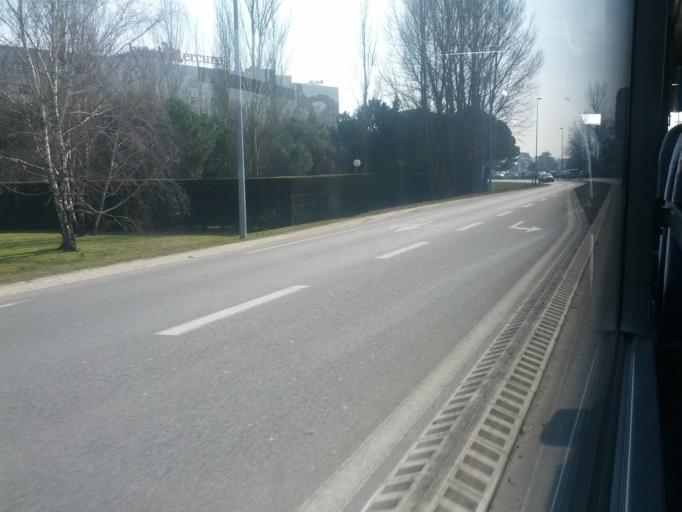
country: FR
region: Aquitaine
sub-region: Departement de la Gironde
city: Le Haillan
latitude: 44.8361
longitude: -0.6937
